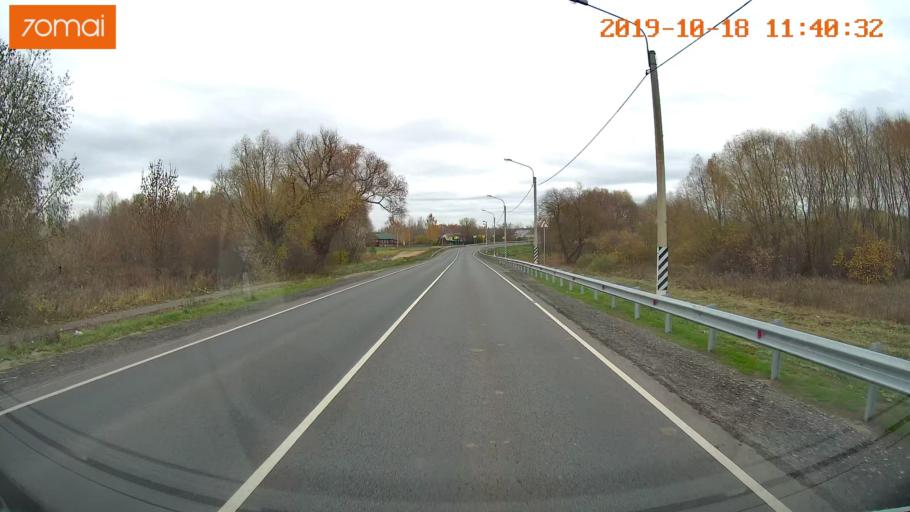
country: RU
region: Rjazan
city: Oktyabr'skiy
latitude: 54.1804
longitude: 38.8922
